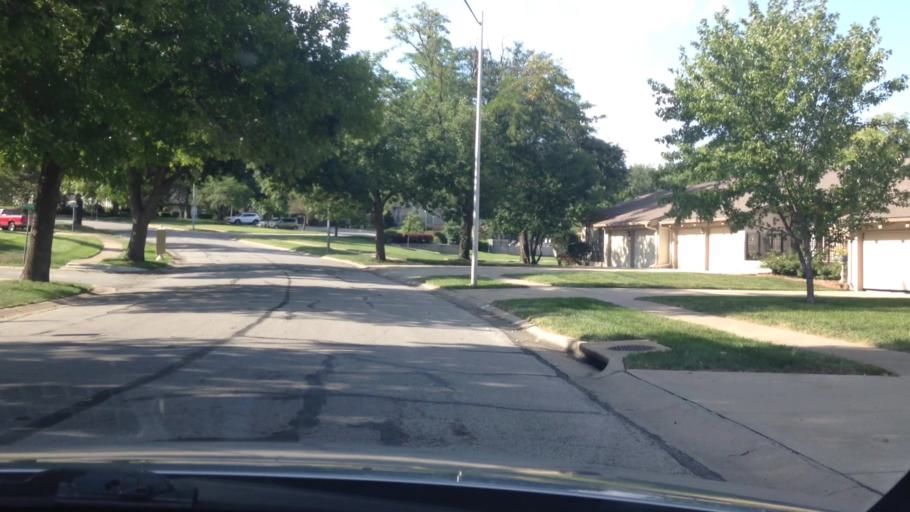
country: US
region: Missouri
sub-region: Jackson County
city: Grandview
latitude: 38.8918
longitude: -94.5903
